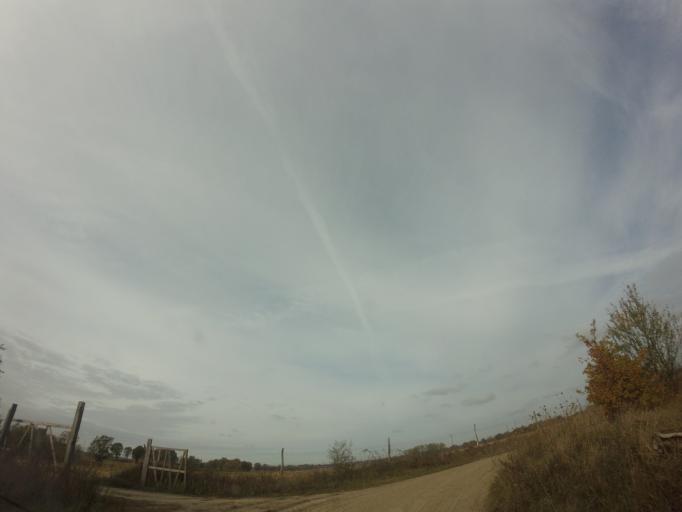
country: PL
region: West Pomeranian Voivodeship
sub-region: Powiat choszczenski
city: Drawno
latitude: 53.2377
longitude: 15.7288
